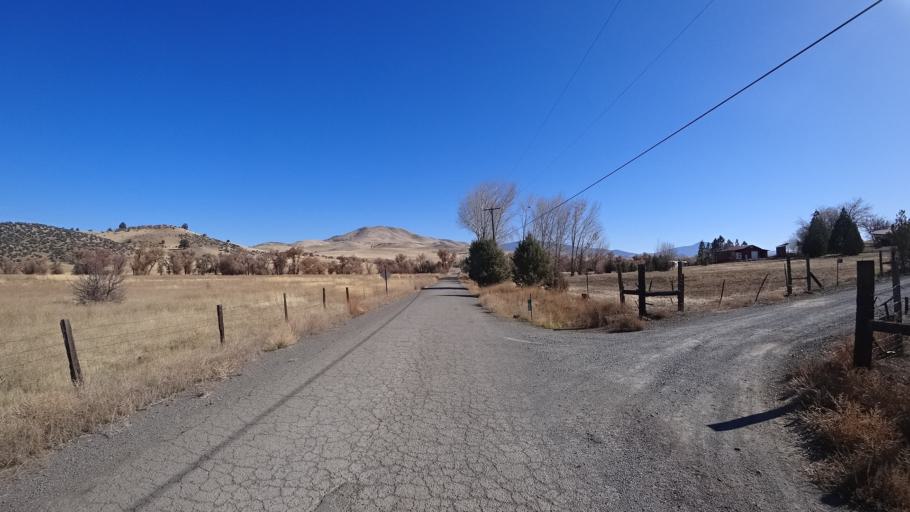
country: US
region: California
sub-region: Siskiyou County
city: Montague
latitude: 41.8479
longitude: -122.4586
